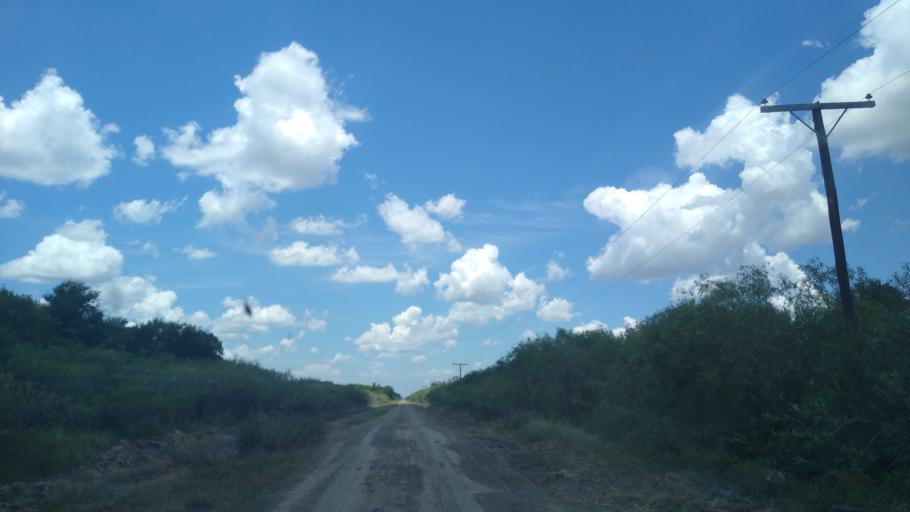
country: AR
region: Chaco
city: Presidencia Roque Saenz Pena
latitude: -26.7409
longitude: -60.3334
